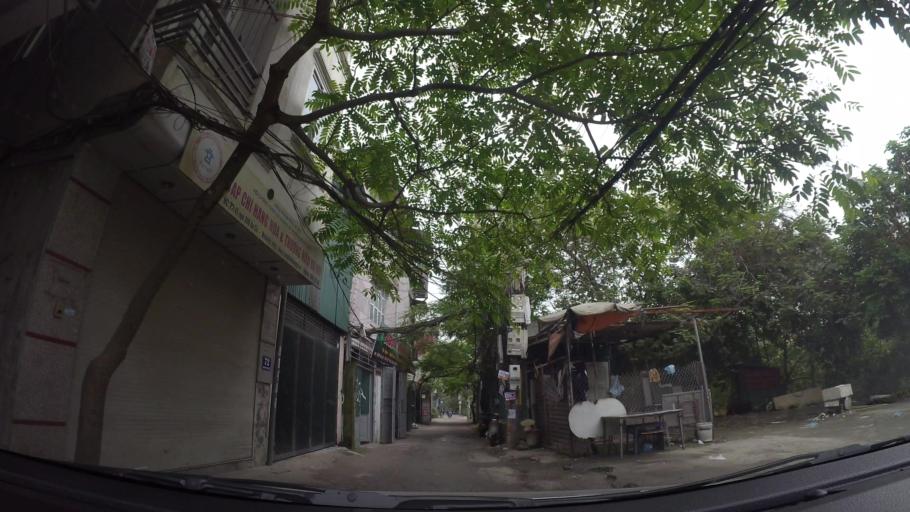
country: VN
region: Ha Noi
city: Tay Ho
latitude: 21.0659
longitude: 105.8323
